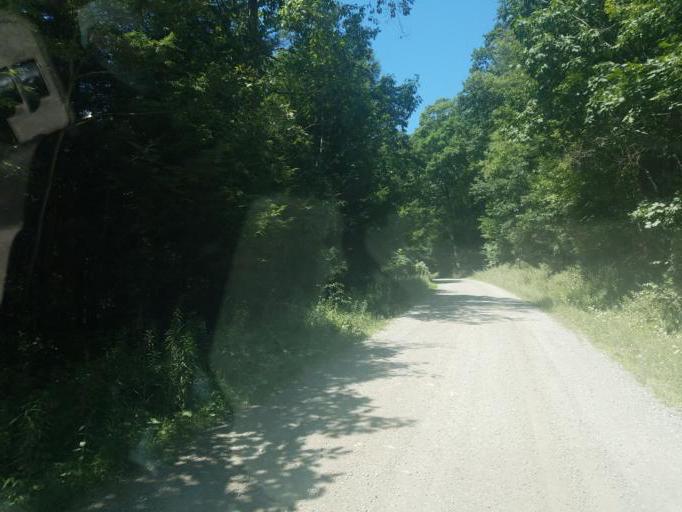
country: US
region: Pennsylvania
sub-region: Clarion County
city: Clarion
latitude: 41.1766
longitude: -79.4462
